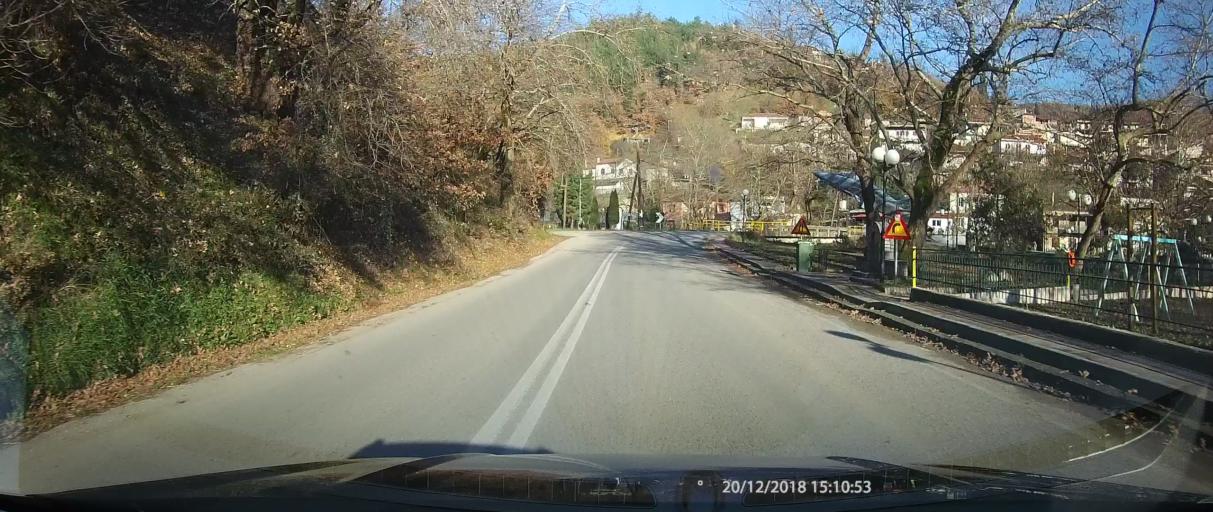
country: GR
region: Central Greece
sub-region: Nomos Fthiotidos
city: Makrakomi
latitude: 38.9475
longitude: 21.9549
